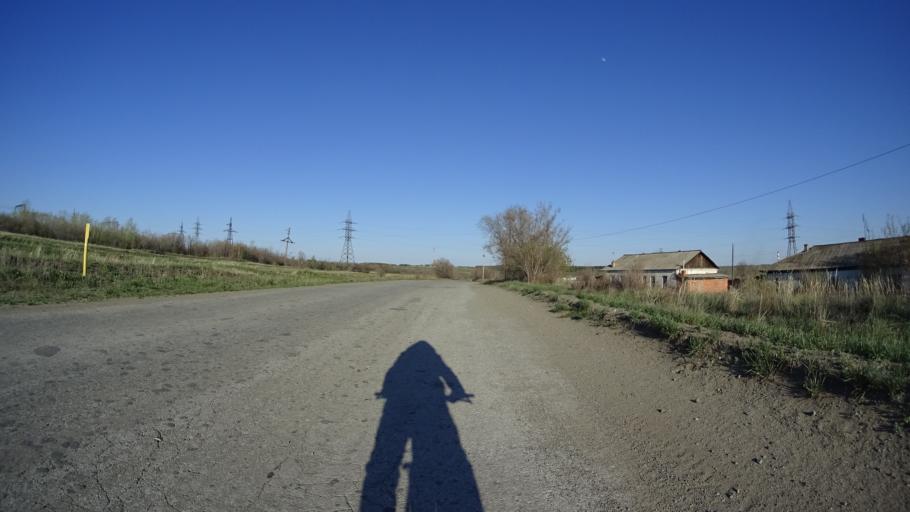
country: RU
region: Chelyabinsk
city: Troitsk
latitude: 54.0764
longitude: 61.6052
